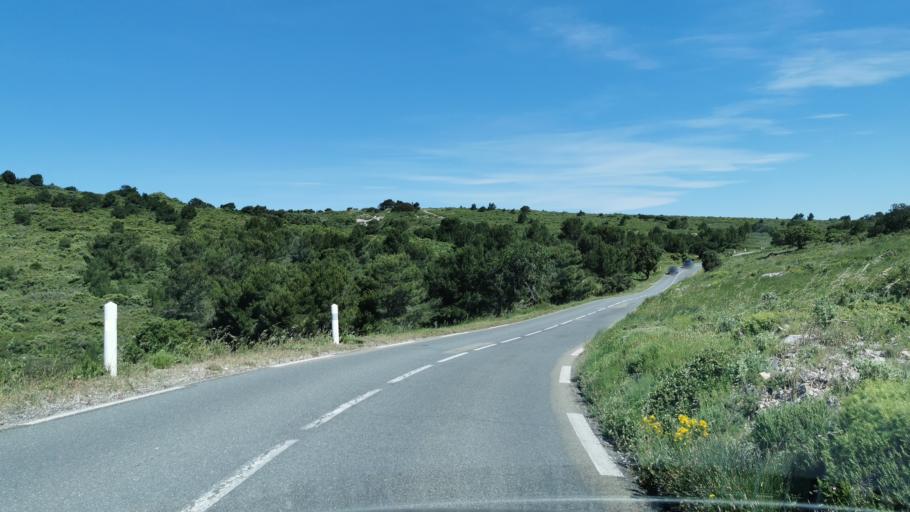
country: FR
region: Languedoc-Roussillon
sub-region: Departement de l'Aude
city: Armissan
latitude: 43.1649
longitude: 3.1327
